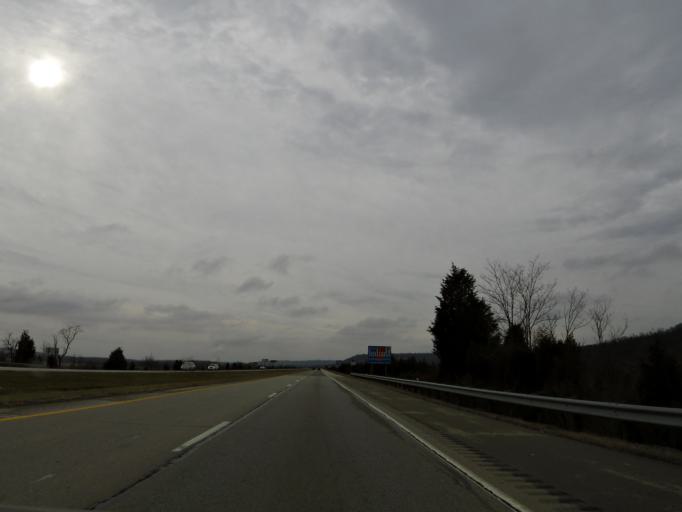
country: US
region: Indiana
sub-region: Dearborn County
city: Hidden Valley
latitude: 39.1464
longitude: -84.8193
